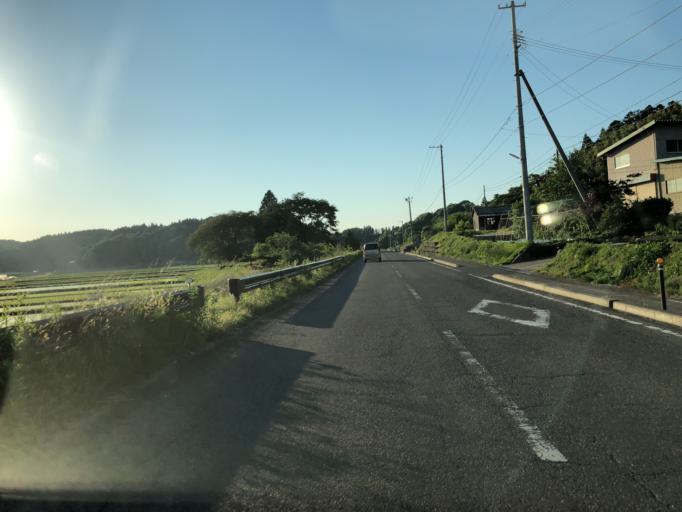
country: JP
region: Fukushima
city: Ishikawa
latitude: 37.0891
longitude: 140.4139
